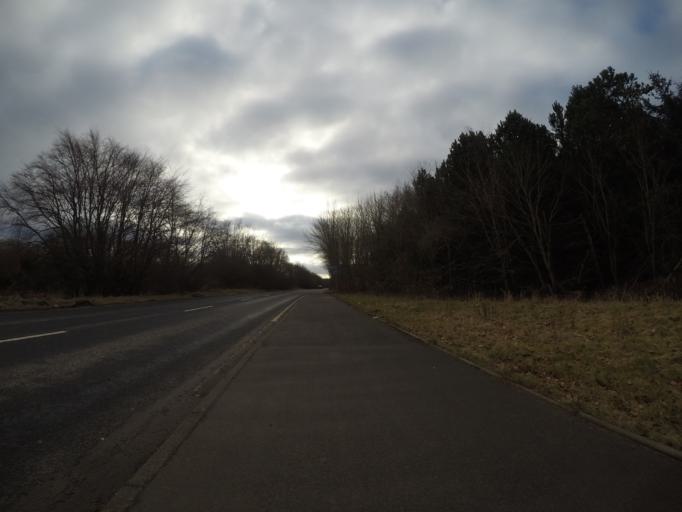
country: GB
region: Scotland
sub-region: North Ayrshire
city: Irvine
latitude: 55.5914
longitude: -4.6516
